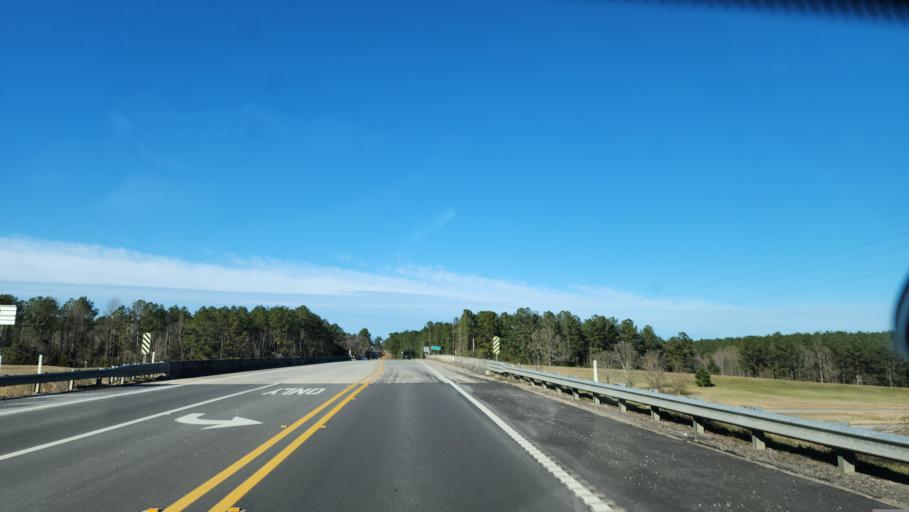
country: US
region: Mississippi
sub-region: Wayne County
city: Waynesboro
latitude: 31.7038
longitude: -88.6442
